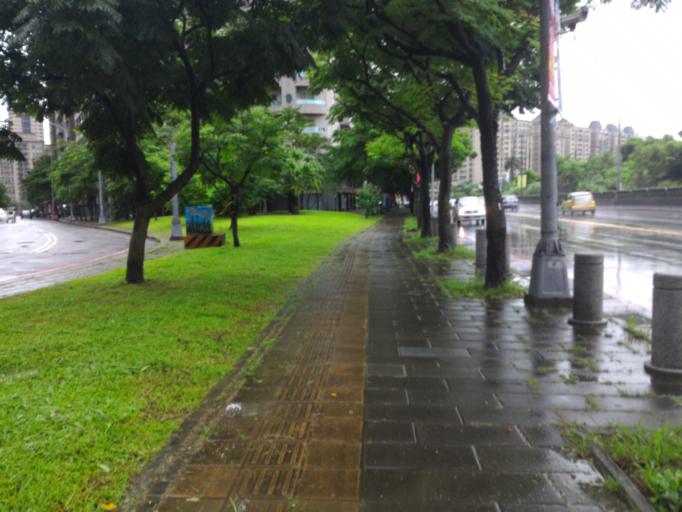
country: TW
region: Taiwan
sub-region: Taoyuan
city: Taoyuan
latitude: 24.9414
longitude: 121.3714
